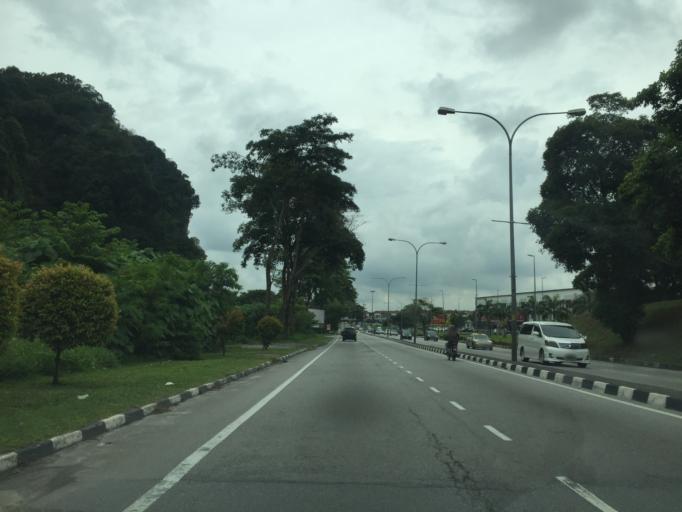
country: MY
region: Perak
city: Ipoh
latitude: 4.5627
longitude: 101.1128
